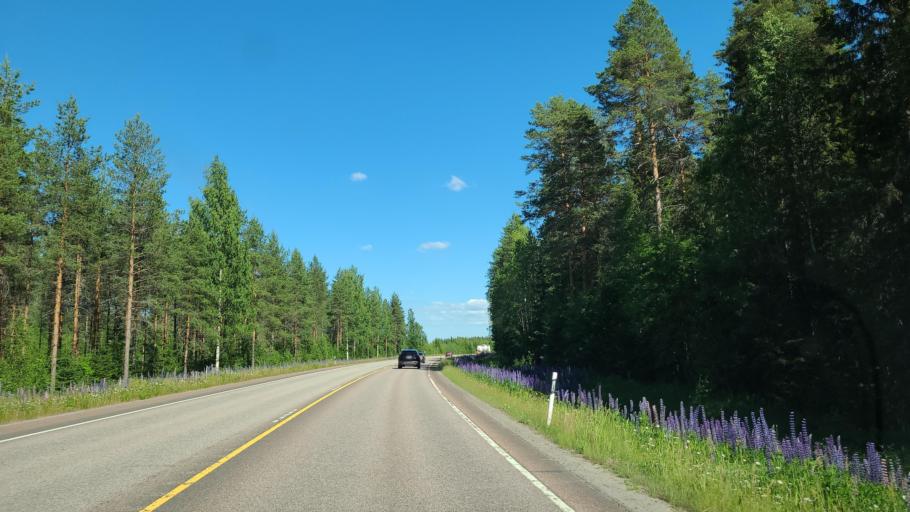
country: FI
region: Central Finland
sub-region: Jyvaeskylae
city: Petaejaevesi
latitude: 62.2717
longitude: 25.4096
